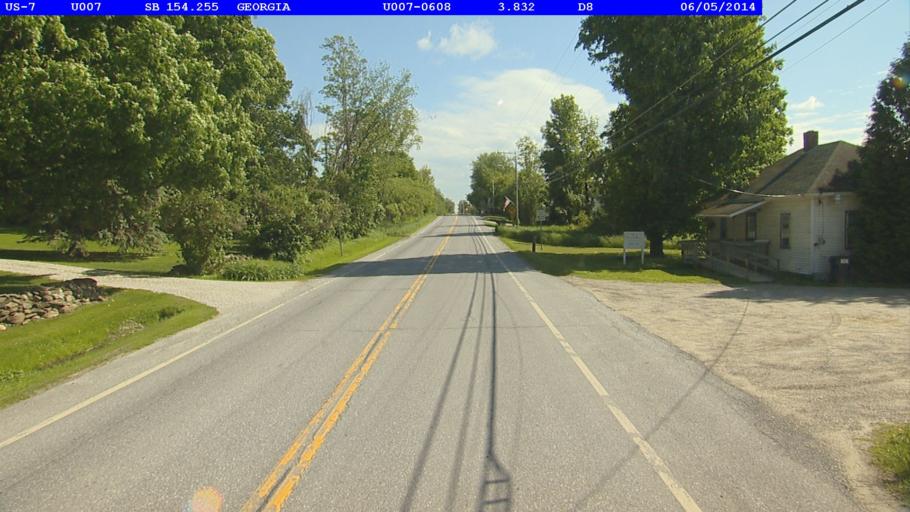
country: US
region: Vermont
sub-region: Chittenden County
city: Milton
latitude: 44.7266
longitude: -73.1181
